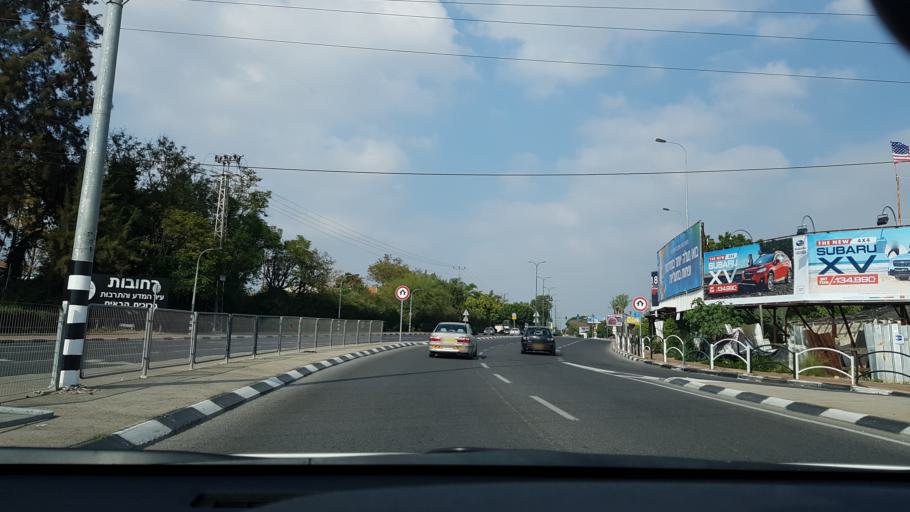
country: IL
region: Central District
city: Mazkeret Batya
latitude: 31.8711
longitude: 34.8195
